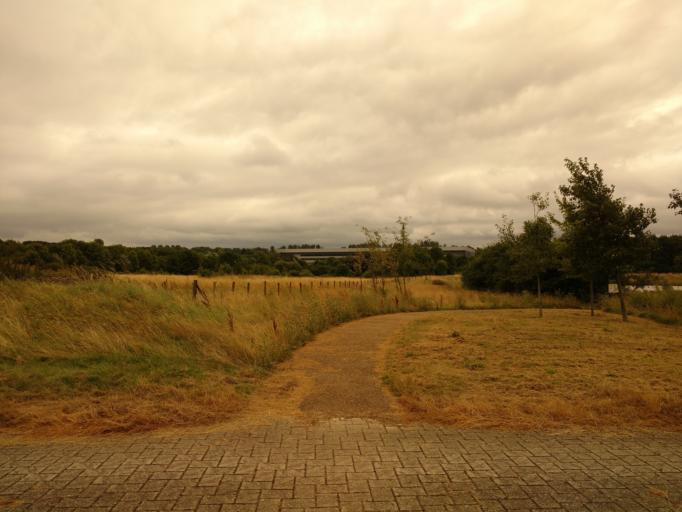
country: GB
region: England
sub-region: Milton Keynes
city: Shenley Church End
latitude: 51.9928
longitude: -0.7952
